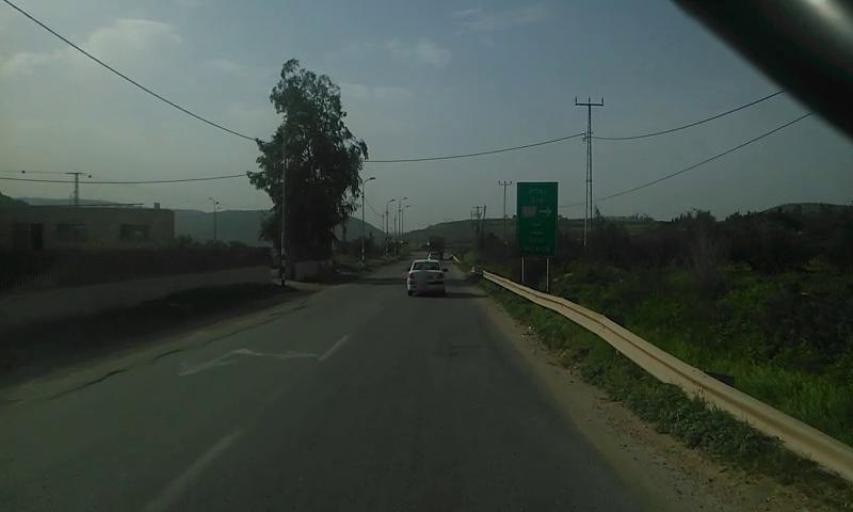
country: PS
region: West Bank
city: Dayr Sharaf
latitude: 32.2647
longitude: 35.1700
